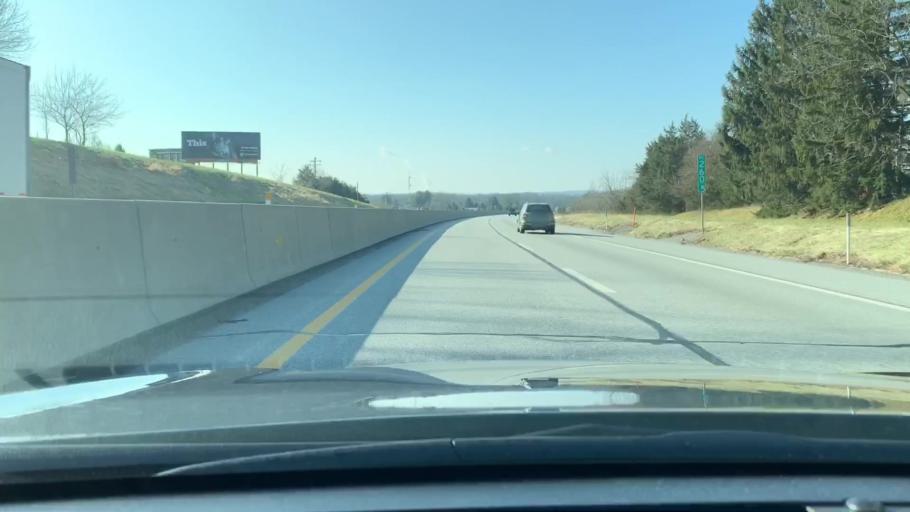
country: US
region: Pennsylvania
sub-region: Lebanon County
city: Campbelltown
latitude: 40.2109
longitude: -76.5419
